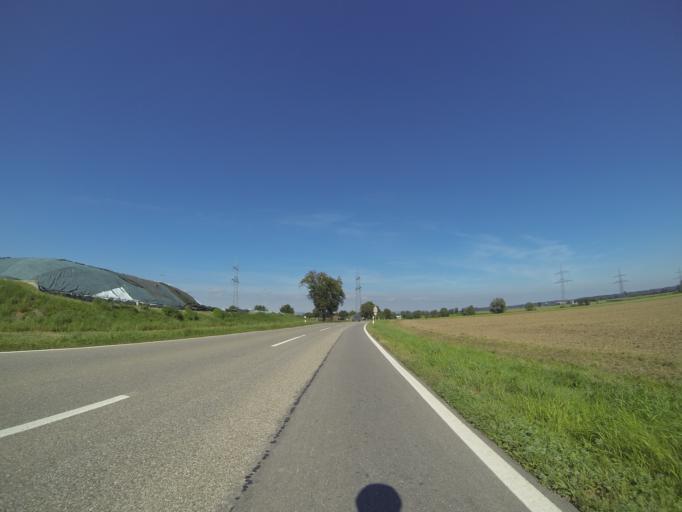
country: DE
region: Baden-Wuerttemberg
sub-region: Tuebingen Region
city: Achstetten
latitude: 48.2928
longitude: 9.9059
